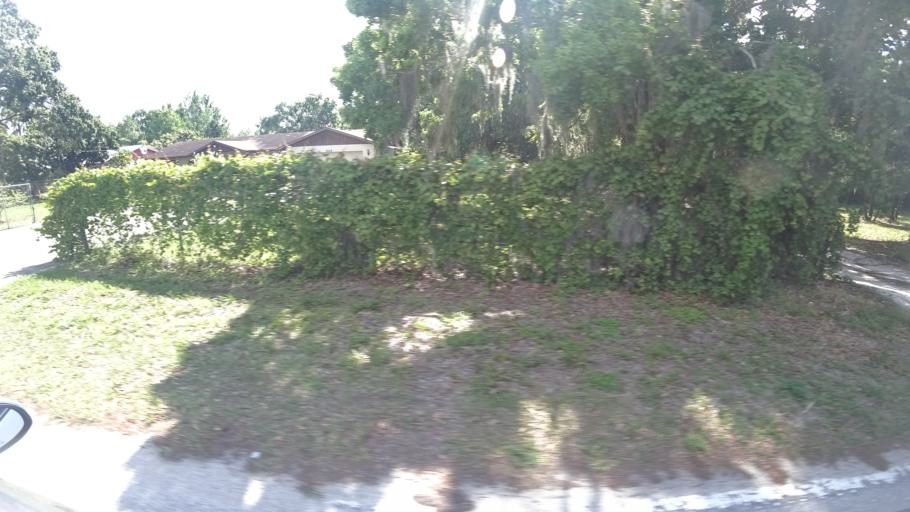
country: US
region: Florida
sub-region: Manatee County
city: Whitfield
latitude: 27.4120
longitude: -82.5289
